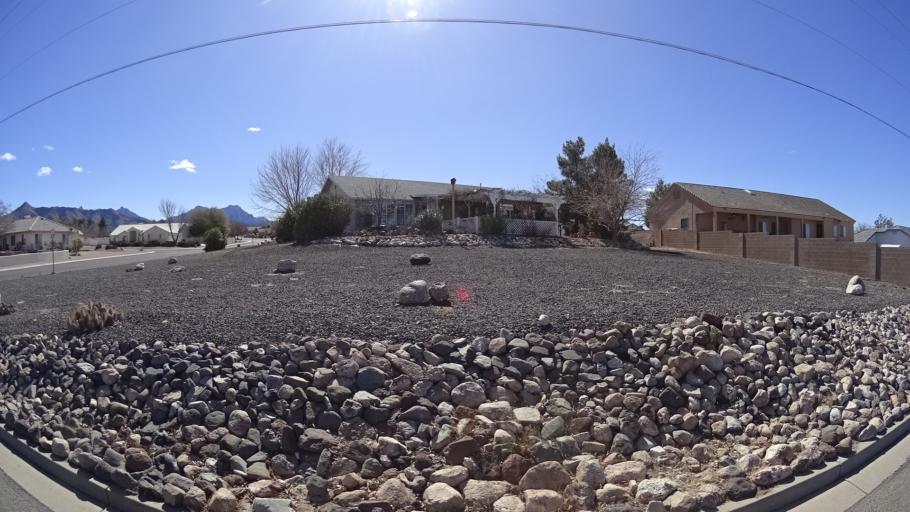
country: US
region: Arizona
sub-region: Mohave County
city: Kingman
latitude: 35.1958
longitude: -113.9805
